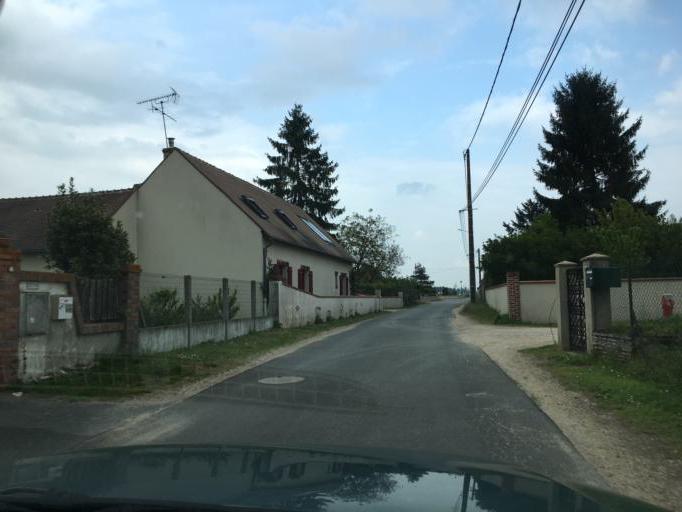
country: FR
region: Centre
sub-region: Departement du Loiret
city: Dry
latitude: 47.7933
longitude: 1.7127
